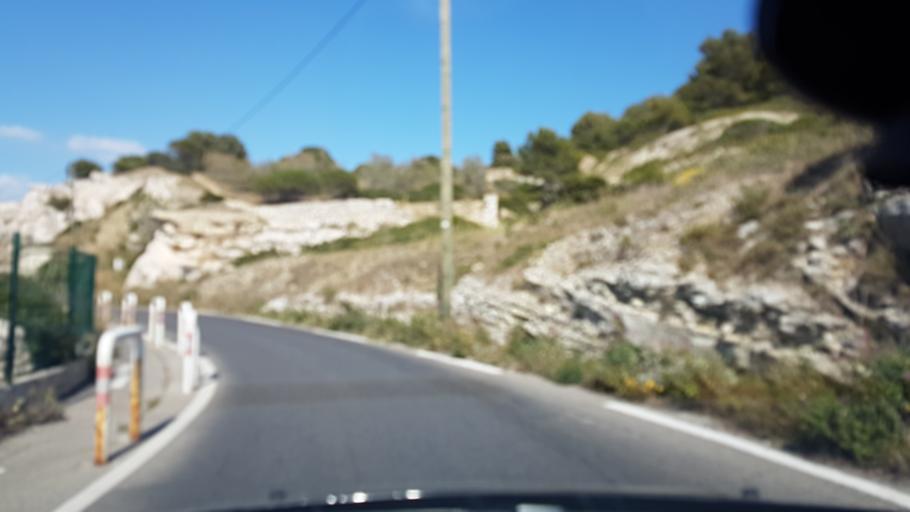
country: FR
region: Provence-Alpes-Cote d'Azur
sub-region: Departement des Bouches-du-Rhone
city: Marseille 08
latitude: 43.2278
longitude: 5.3522
